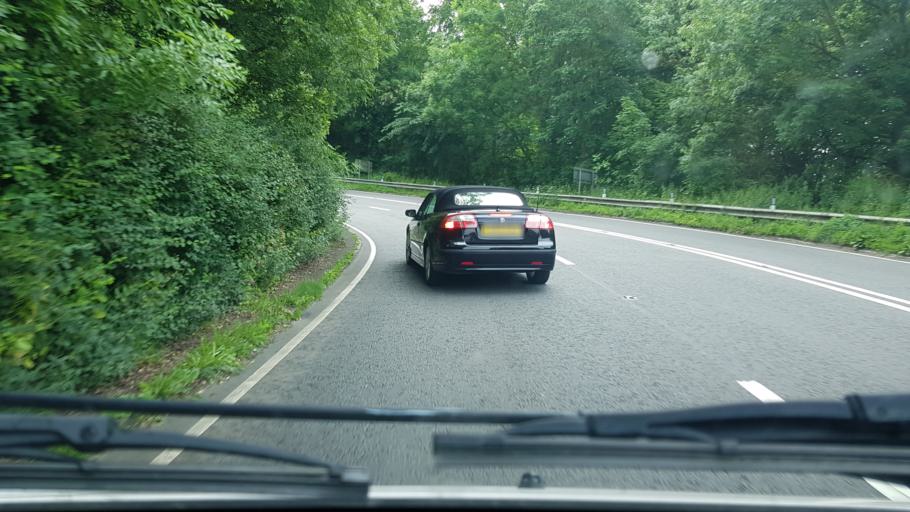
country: GB
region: England
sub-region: Worcestershire
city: Broadway
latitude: 52.0317
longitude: -1.8323
